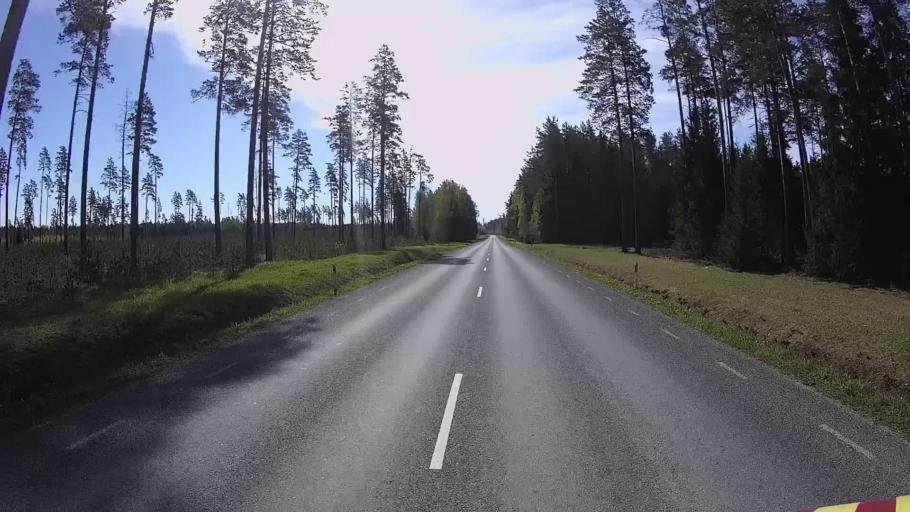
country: EE
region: Polvamaa
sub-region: Polva linn
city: Polva
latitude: 58.1702
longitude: 27.1384
